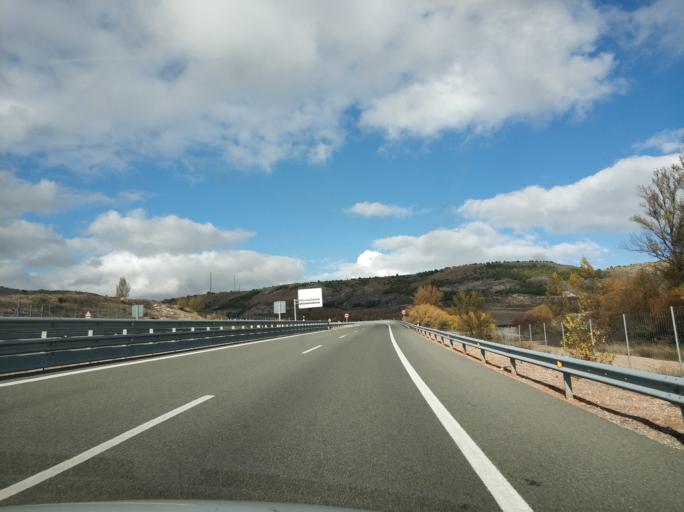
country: ES
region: Castille and Leon
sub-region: Provincia de Soria
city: Medinaceli
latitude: 41.1862
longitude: -2.4310
